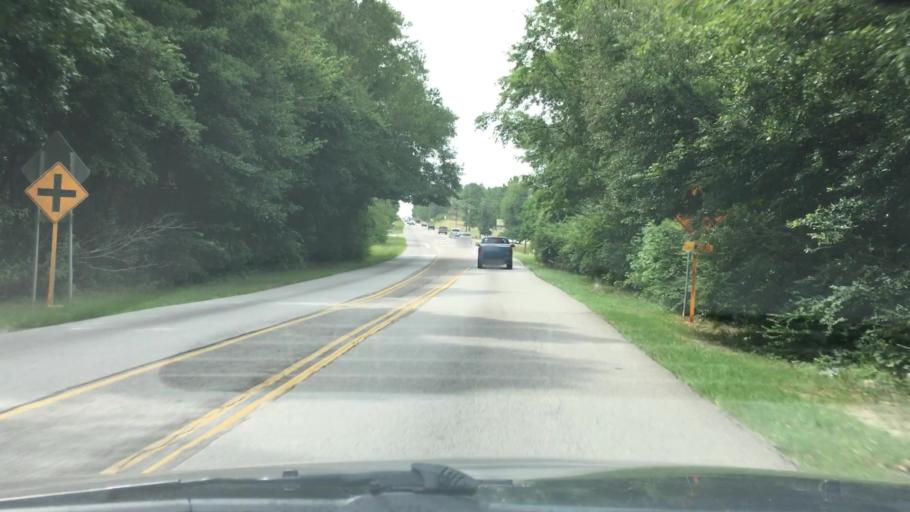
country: US
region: South Carolina
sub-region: Aiken County
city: Warrenville
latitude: 33.5564
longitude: -81.7788
